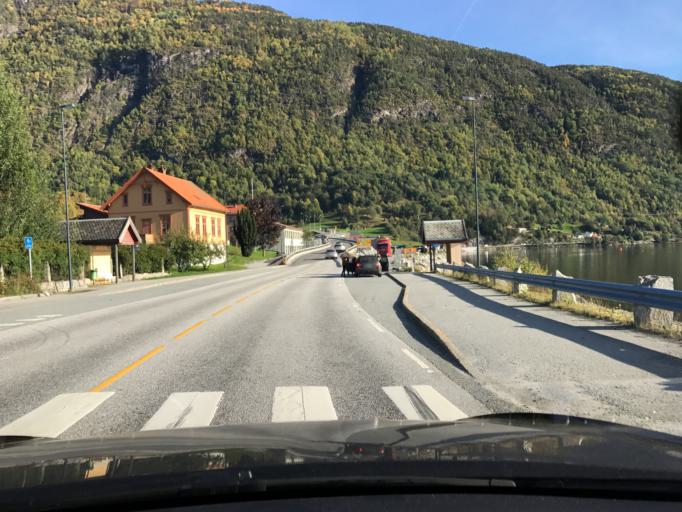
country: NO
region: Sogn og Fjordane
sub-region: Sogndal
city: Sogndalsfjora
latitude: 61.2321
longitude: 7.1149
